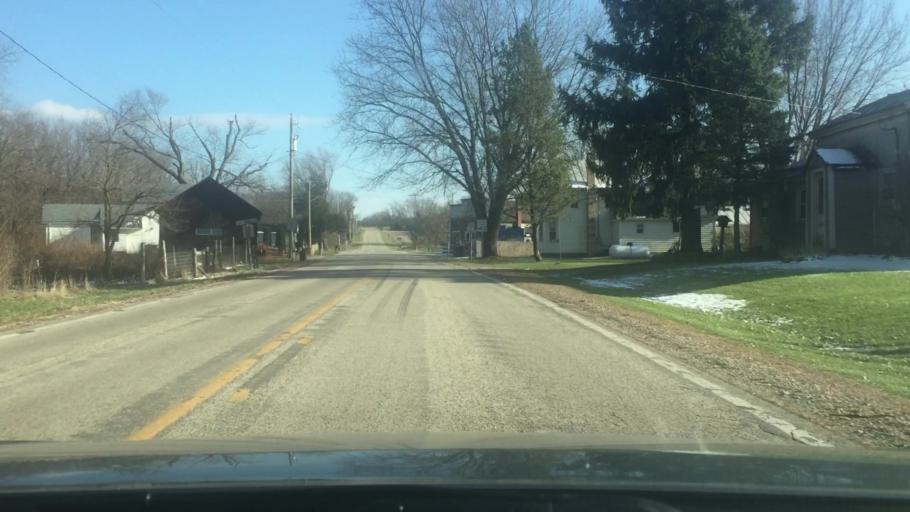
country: US
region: Wisconsin
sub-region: Jefferson County
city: Palmyra
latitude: 42.9367
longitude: -88.5877
